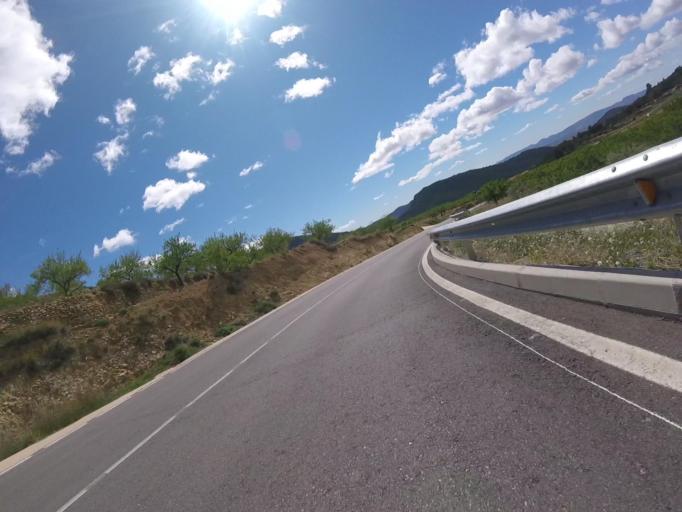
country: ES
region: Valencia
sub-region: Provincia de Castello
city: Culla
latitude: 40.2999
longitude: -0.1200
